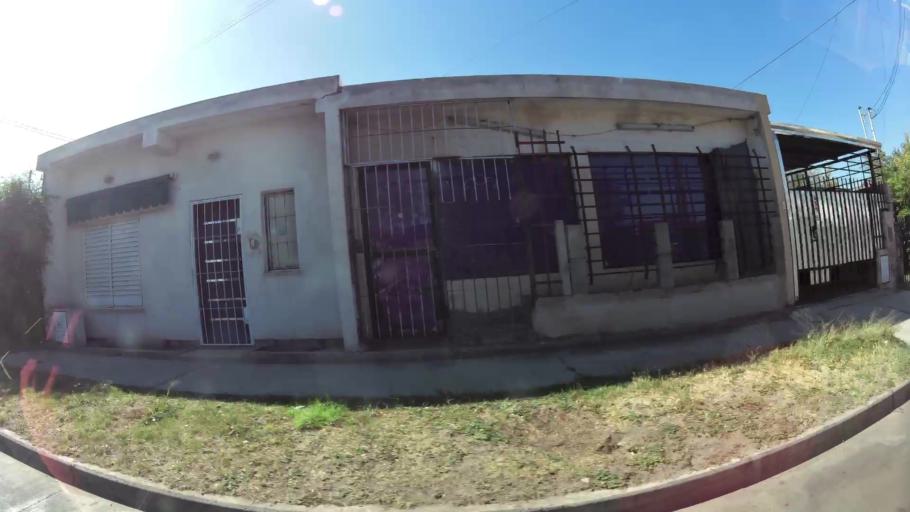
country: AR
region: Cordoba
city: Villa Allende
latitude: -31.3465
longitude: -64.2431
